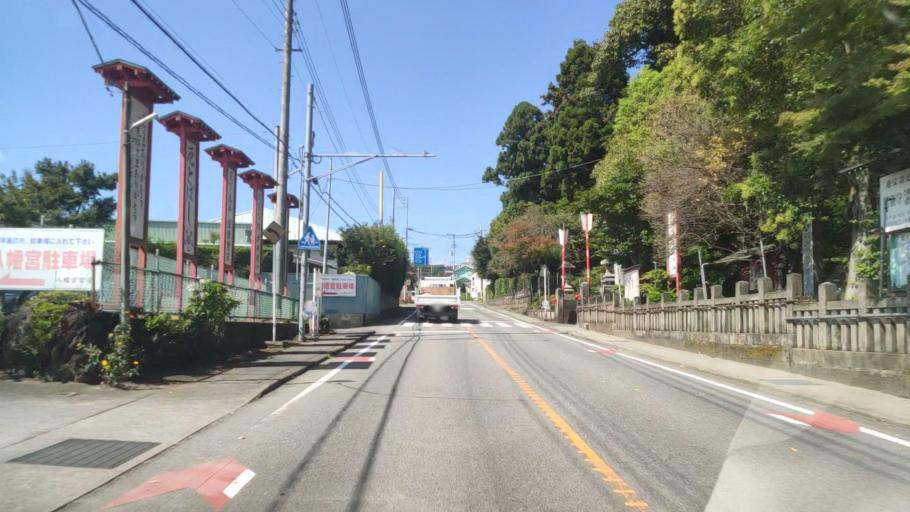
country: JP
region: Gunma
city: Shibukawa
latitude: 36.5013
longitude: 138.9902
